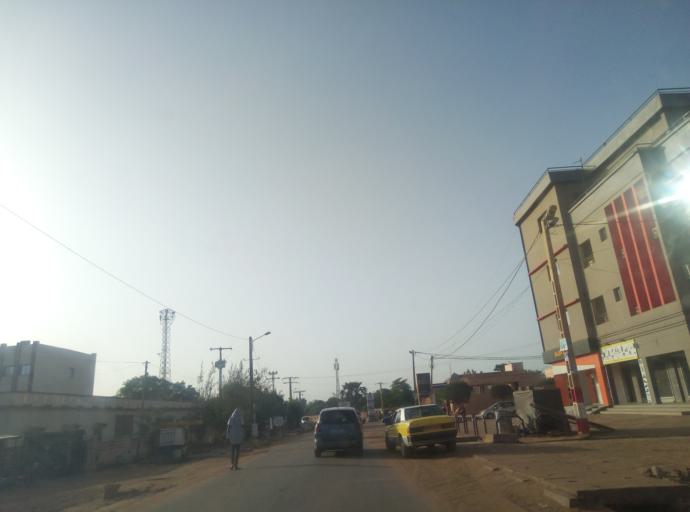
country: ML
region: Bamako
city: Bamako
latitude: 12.6097
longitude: -7.9728
